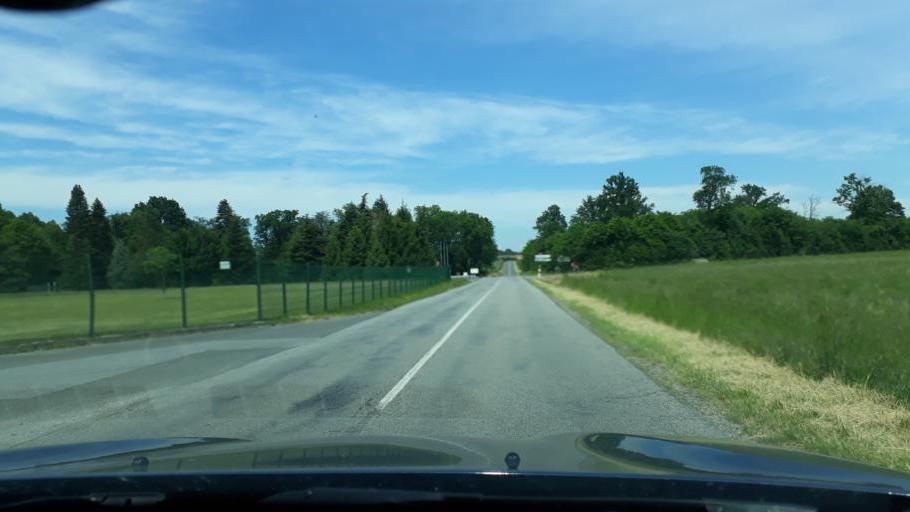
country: FR
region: Centre
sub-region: Departement du Loiret
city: Boiscommun
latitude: 48.0450
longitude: 2.3022
